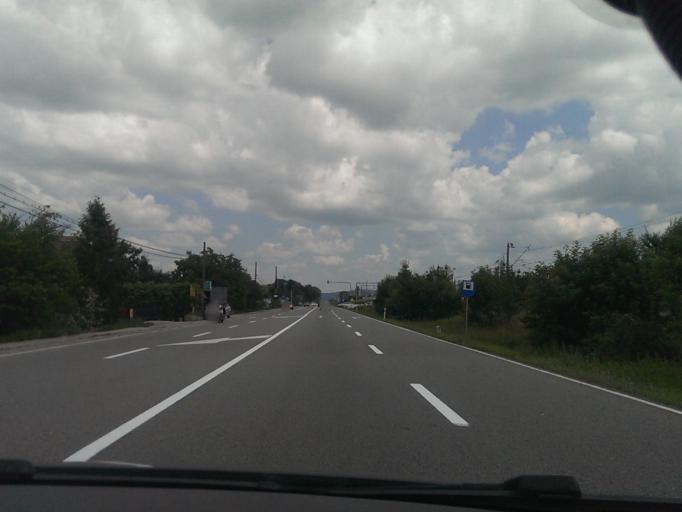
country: RO
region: Cluj
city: Jucu Herghelia
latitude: 46.8577
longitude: 23.7601
